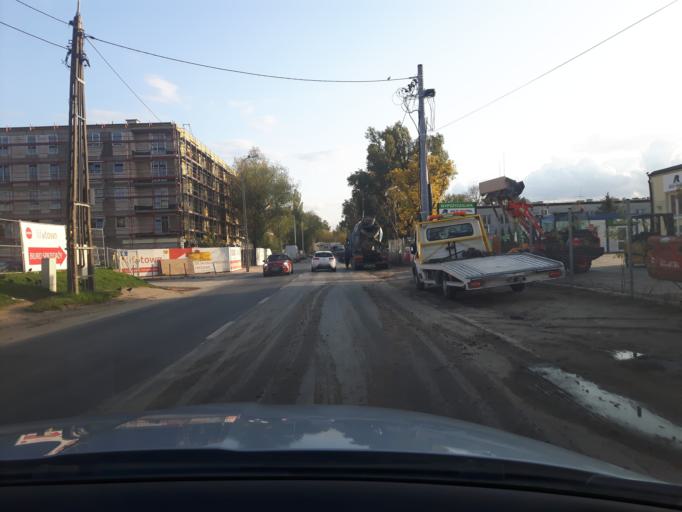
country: PL
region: Masovian Voivodeship
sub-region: Warszawa
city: Wlochy
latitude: 52.1612
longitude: 20.9923
